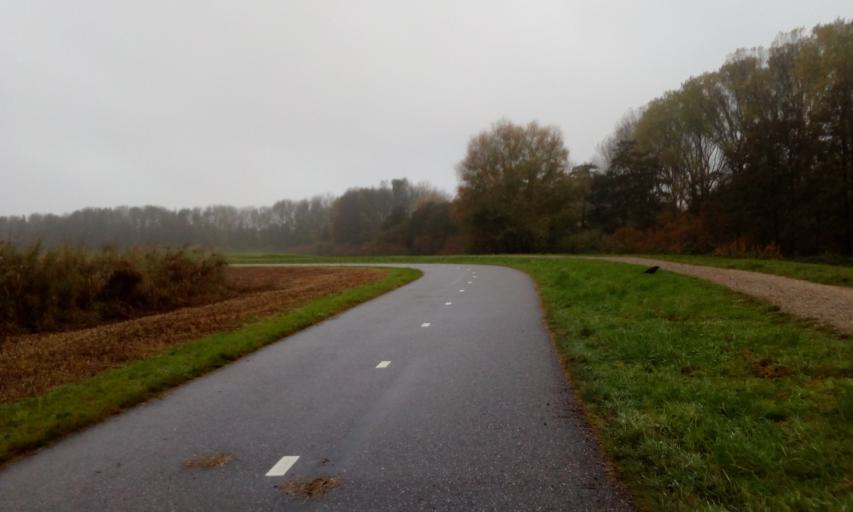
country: NL
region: South Holland
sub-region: Gemeente Lansingerland
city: Bleiswijk
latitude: 52.0095
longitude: 4.5546
